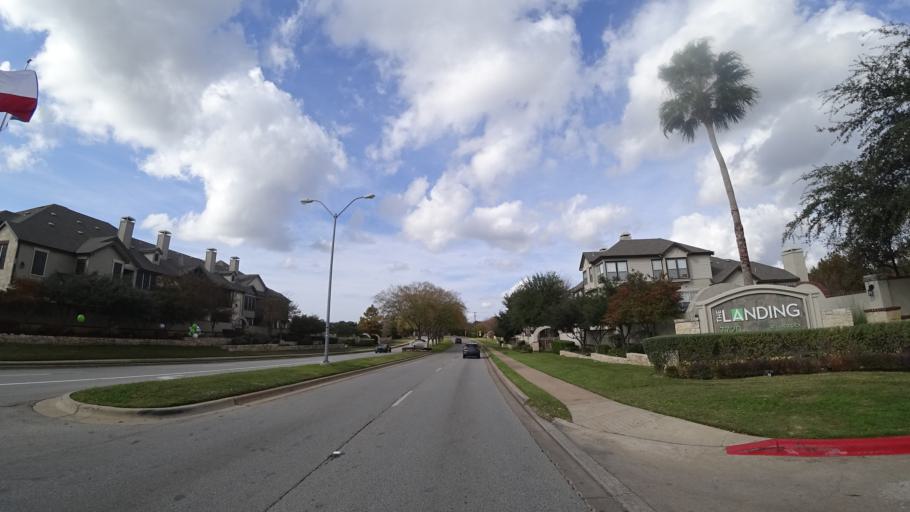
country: US
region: Texas
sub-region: Williamson County
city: Brushy Creek
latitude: 30.5006
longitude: -97.7243
